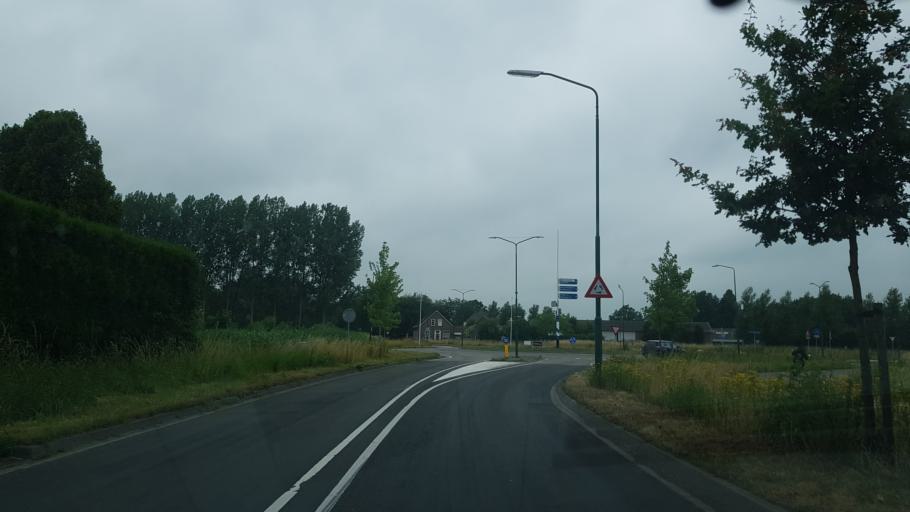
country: NL
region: North Brabant
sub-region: Gemeente Sint-Oedenrode
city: Sint-Oedenrode
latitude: 51.5565
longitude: 5.4727
